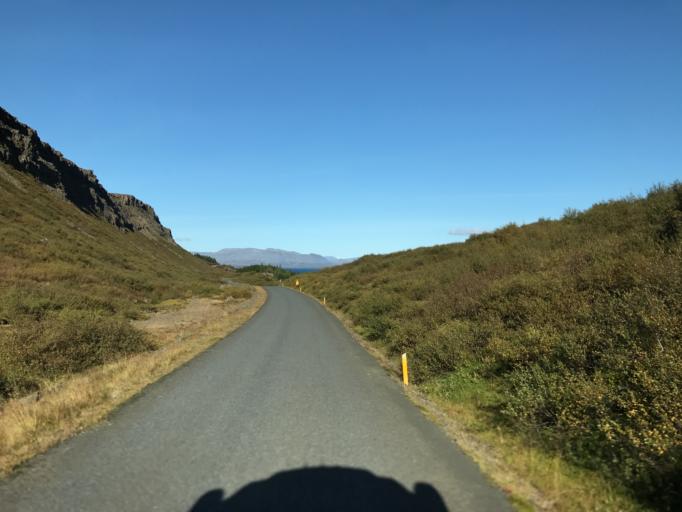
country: IS
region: South
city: Hveragerdi
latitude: 64.1669
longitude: -21.2402
